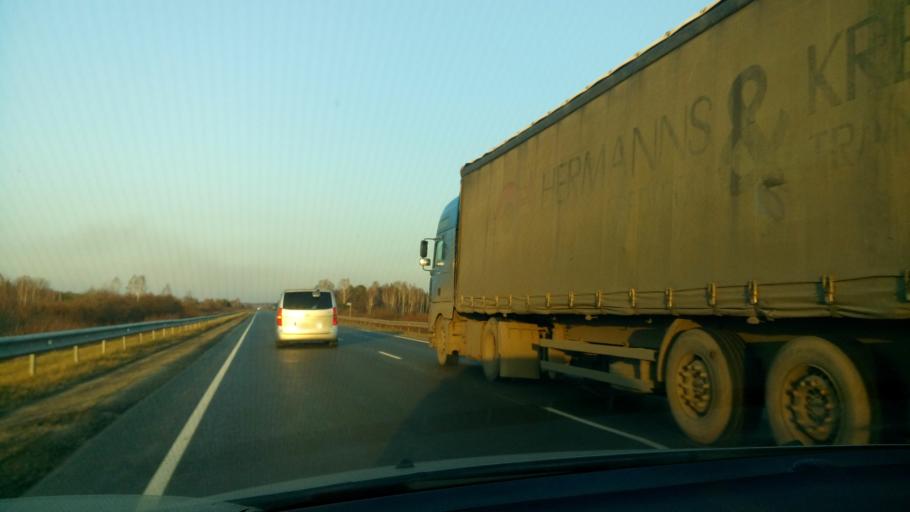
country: RU
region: Sverdlovsk
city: Yelanskiy
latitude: 56.8181
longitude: 62.5429
